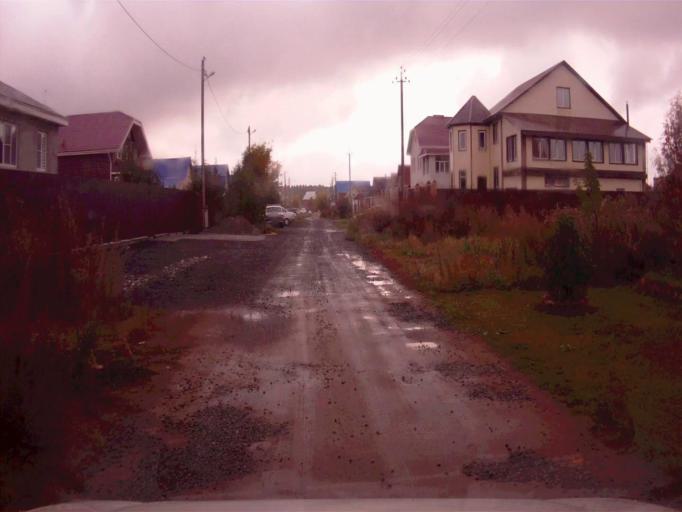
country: RU
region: Chelyabinsk
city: Dolgoderevenskoye
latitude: 55.3071
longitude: 61.3414
